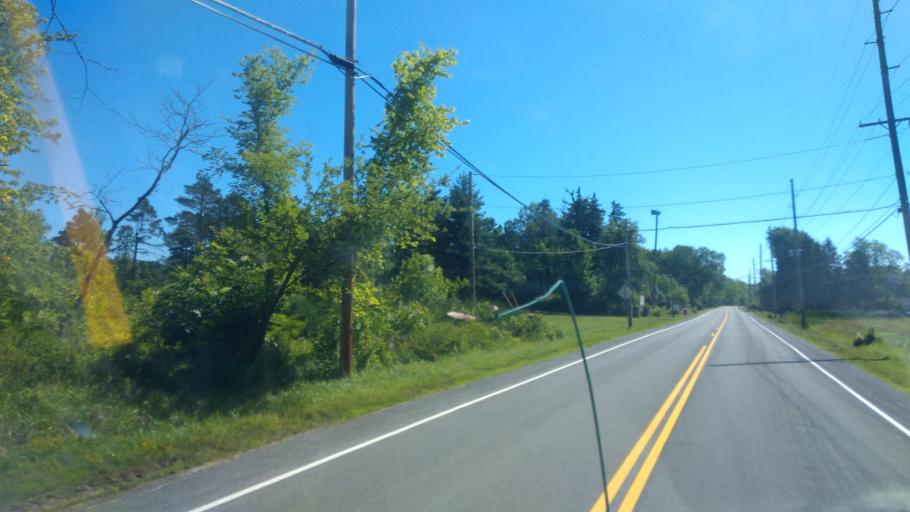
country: US
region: New York
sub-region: Monroe County
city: Webster
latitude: 43.2685
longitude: -77.3991
